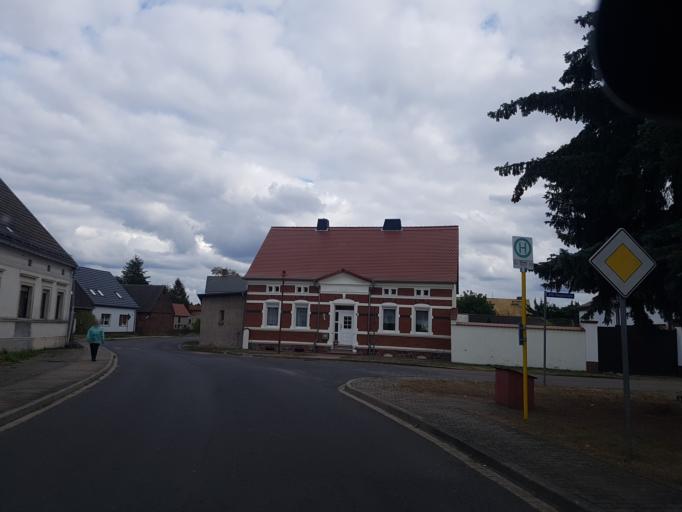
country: DE
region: Saxony-Anhalt
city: Rosslau
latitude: 51.9575
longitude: 12.3017
